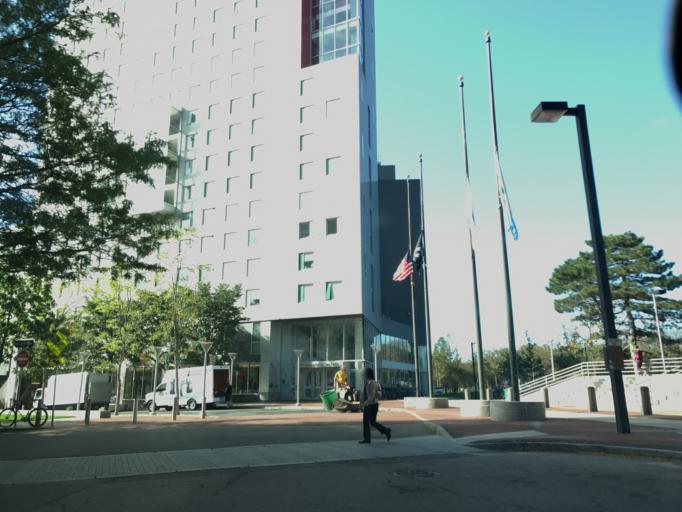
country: US
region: Massachusetts
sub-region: Norfolk County
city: Brookline
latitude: 42.3358
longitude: -71.0886
